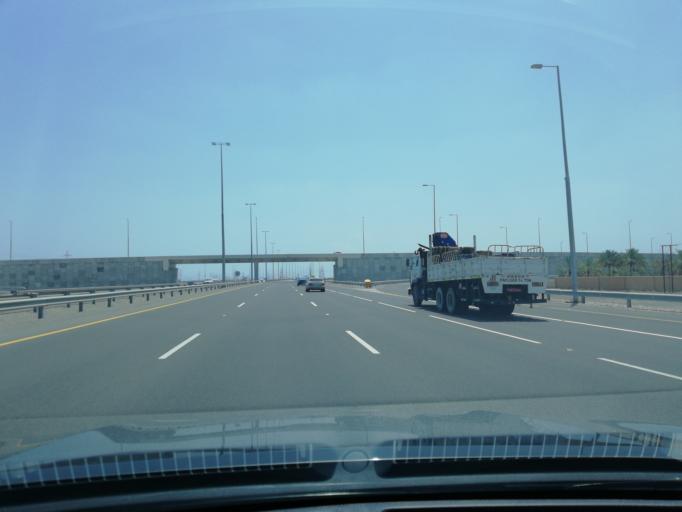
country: OM
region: Al Batinah
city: Barka'
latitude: 23.6313
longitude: 57.9879
